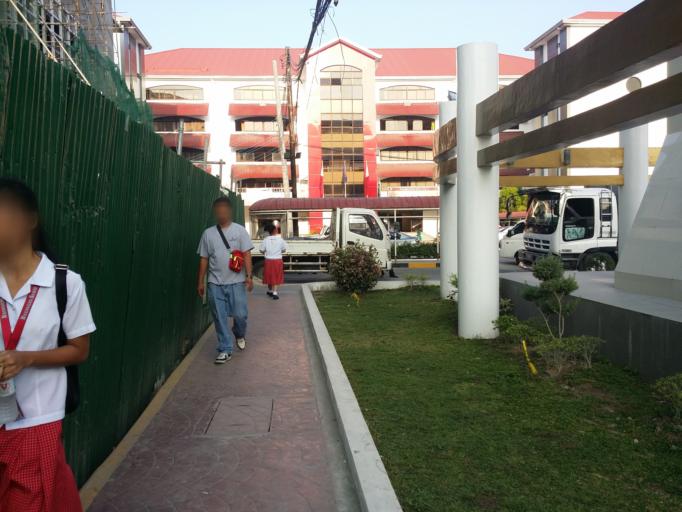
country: PH
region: Calabarzon
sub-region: Province of Batangas
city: Batangas
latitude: 13.7538
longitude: 121.0535
